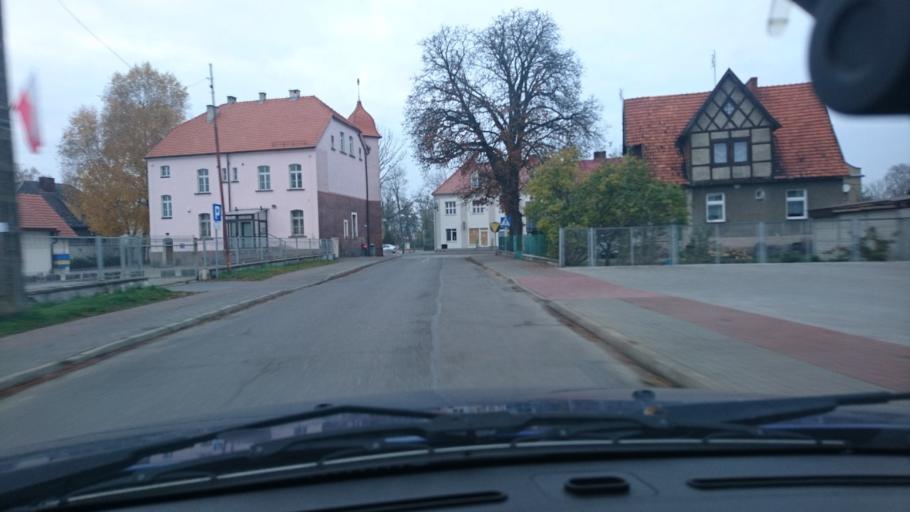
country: PL
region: Greater Poland Voivodeship
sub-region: Powiat ostrowski
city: Odolanow
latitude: 51.5736
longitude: 17.6711
